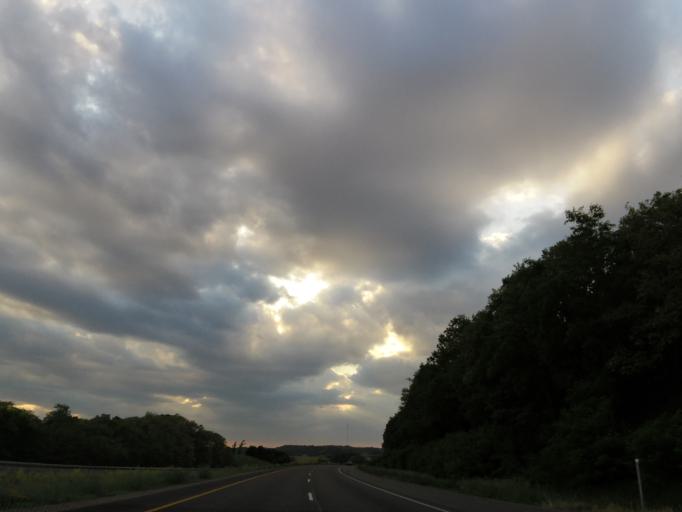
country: US
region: Wisconsin
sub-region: Trempealeau County
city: Osseo
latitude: 44.4798
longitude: -91.1118
